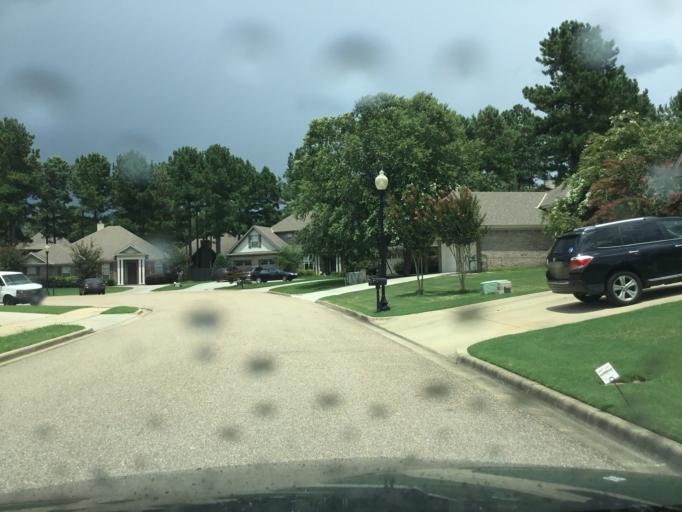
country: US
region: Alabama
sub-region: Montgomery County
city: Pike Road
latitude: 32.3432
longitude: -86.0815
